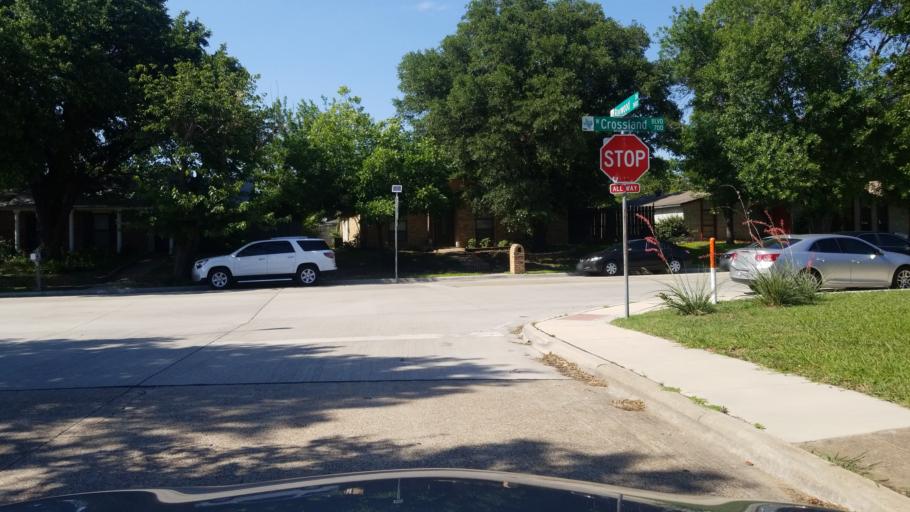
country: US
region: Texas
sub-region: Dallas County
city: Grand Prairie
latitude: 32.6800
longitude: -97.0139
